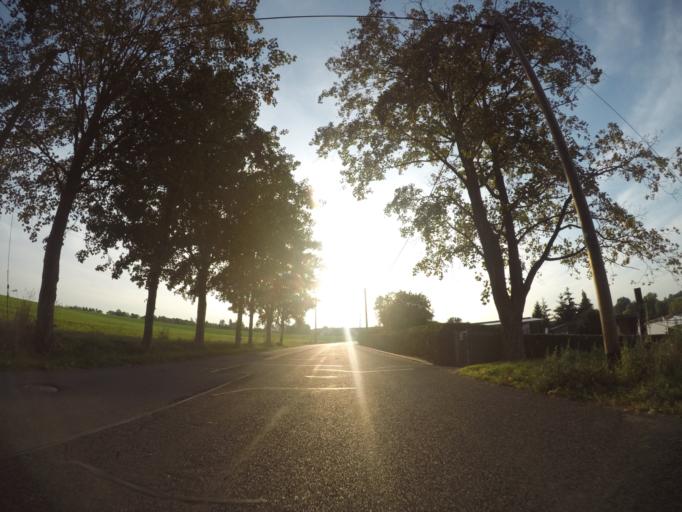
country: DE
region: Thuringia
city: Altkirchen
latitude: 50.9346
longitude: 12.3671
